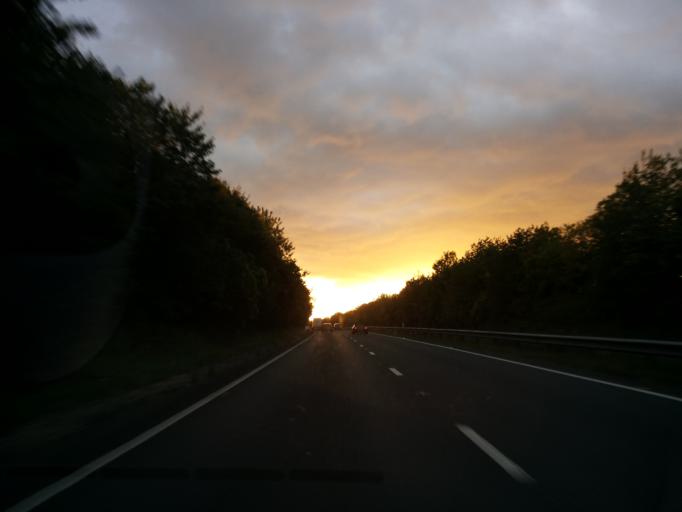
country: GB
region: England
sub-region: Hampshire
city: Abbotts Ann
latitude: 51.2127
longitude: -1.5643
